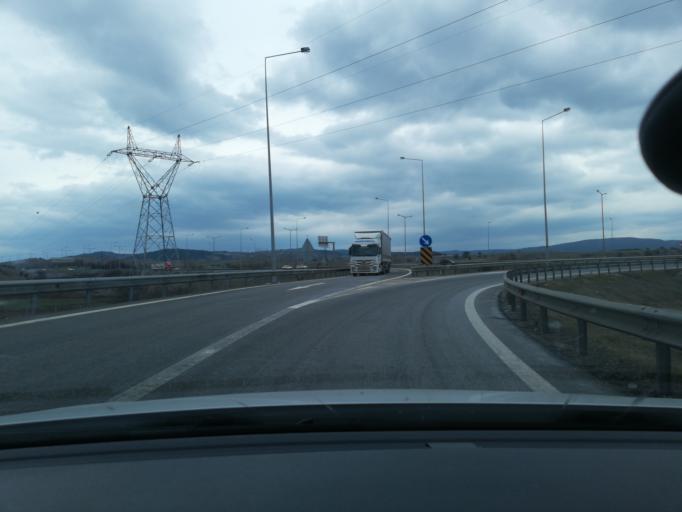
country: TR
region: Bolu
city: Yenicaga
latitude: 40.7624
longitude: 32.0090
